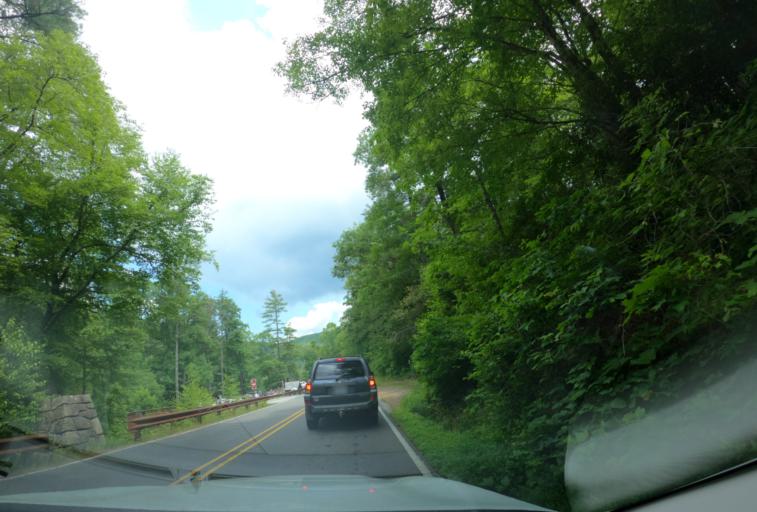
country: US
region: North Carolina
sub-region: Macon County
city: Franklin
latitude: 35.0676
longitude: -83.2382
